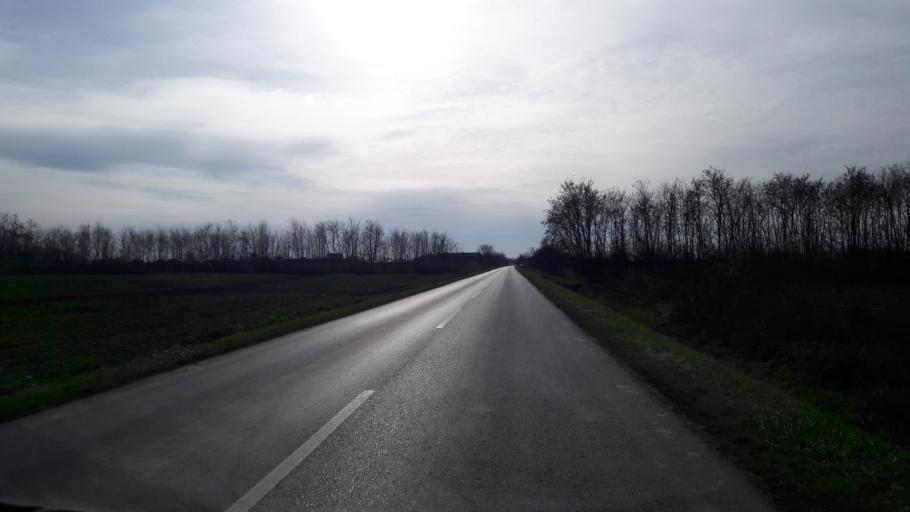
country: HR
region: Osjecko-Baranjska
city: Semeljci
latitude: 45.3166
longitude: 18.5573
